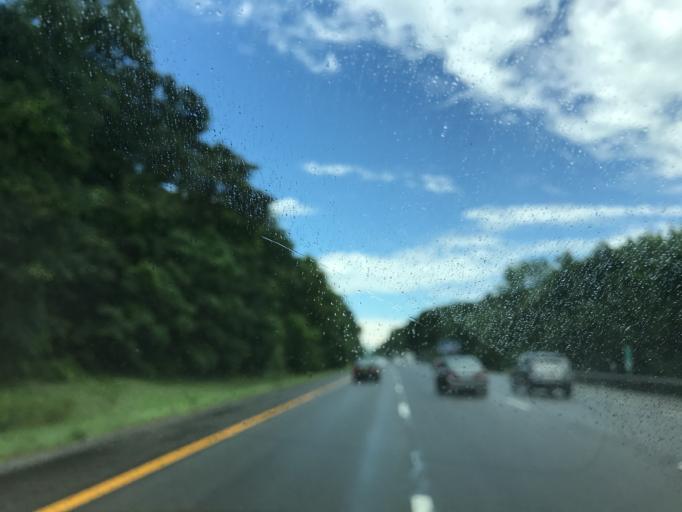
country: US
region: New York
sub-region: Saratoga County
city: Country Knolls
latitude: 42.8457
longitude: -73.7721
